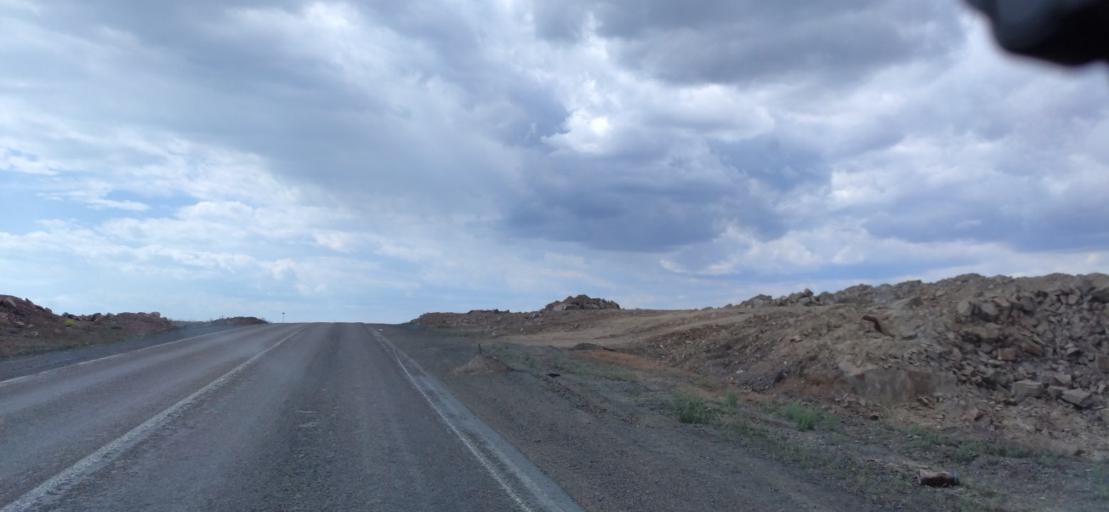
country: KZ
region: Qaraghandy
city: Saryshaghan
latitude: 46.0832
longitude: 73.6053
